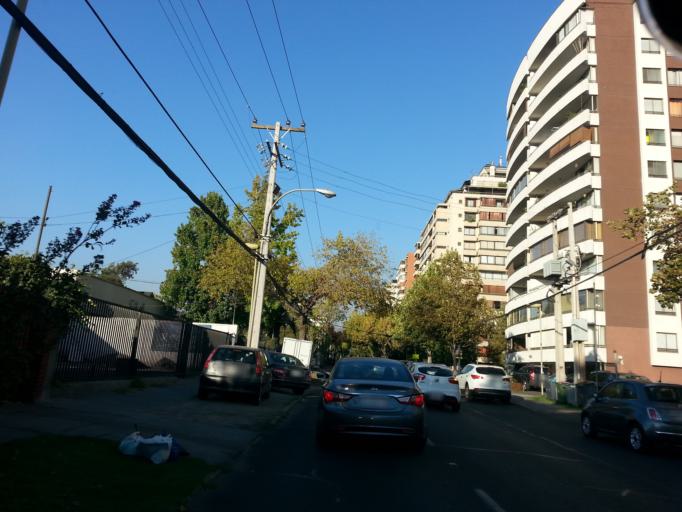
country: CL
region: Santiago Metropolitan
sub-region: Provincia de Santiago
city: Villa Presidente Frei, Nunoa, Santiago, Chile
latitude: -33.4161
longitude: -70.5698
